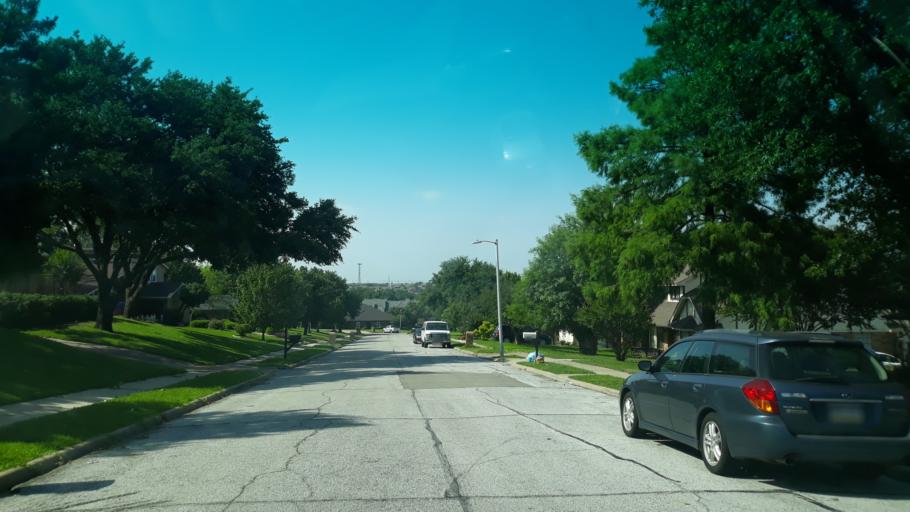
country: US
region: Texas
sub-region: Dallas County
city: Irving
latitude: 32.8615
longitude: -96.9790
